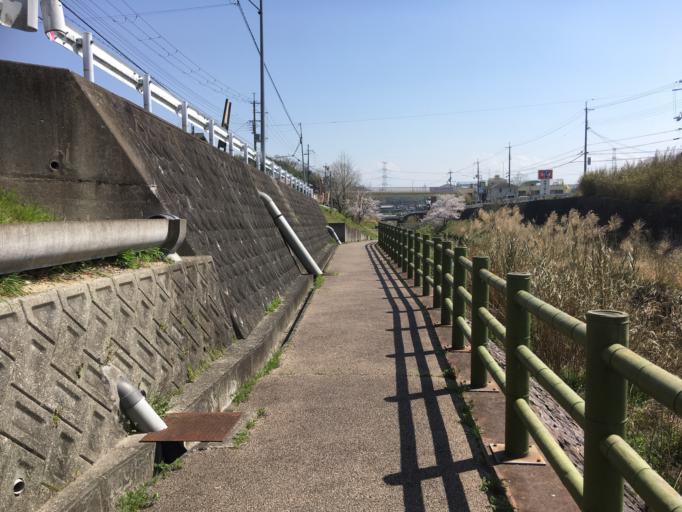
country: JP
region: Nara
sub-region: Ikoma-shi
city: Ikoma
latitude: 34.7429
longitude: 135.7215
